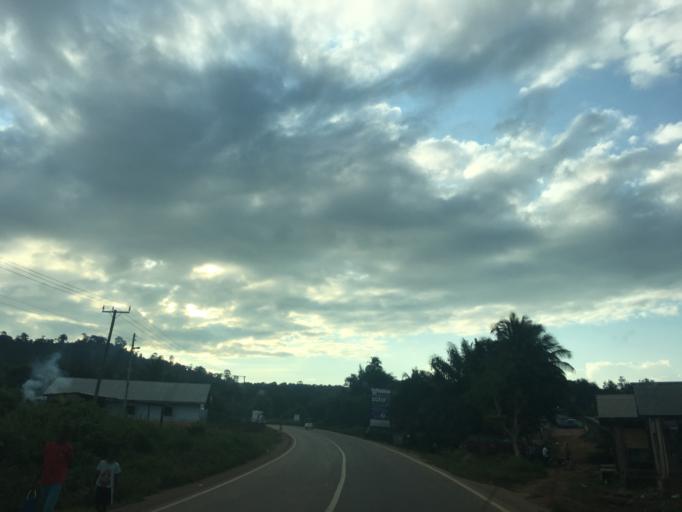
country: GH
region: Western
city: Bibiani
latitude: 6.4632
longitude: -2.3233
